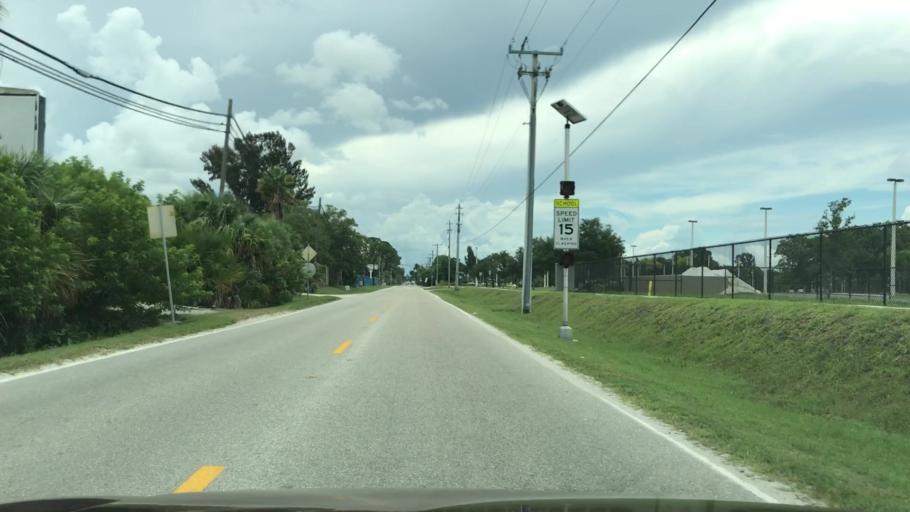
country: US
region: Florida
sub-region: Sarasota County
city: North Sarasota
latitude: 27.3672
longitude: -82.5415
